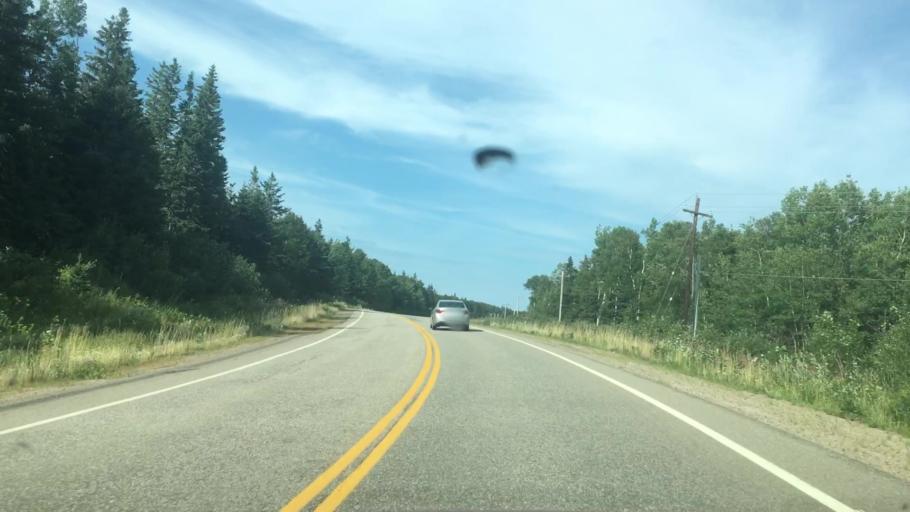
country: CA
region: Nova Scotia
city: Sydney Mines
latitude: 46.7154
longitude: -60.3527
